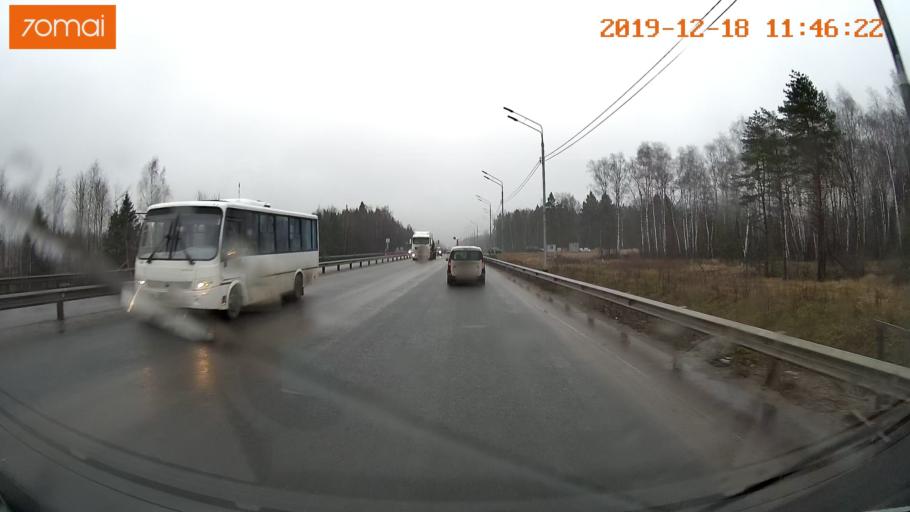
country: RU
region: Moskovskaya
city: Zvenigorod
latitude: 55.7490
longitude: 36.8873
